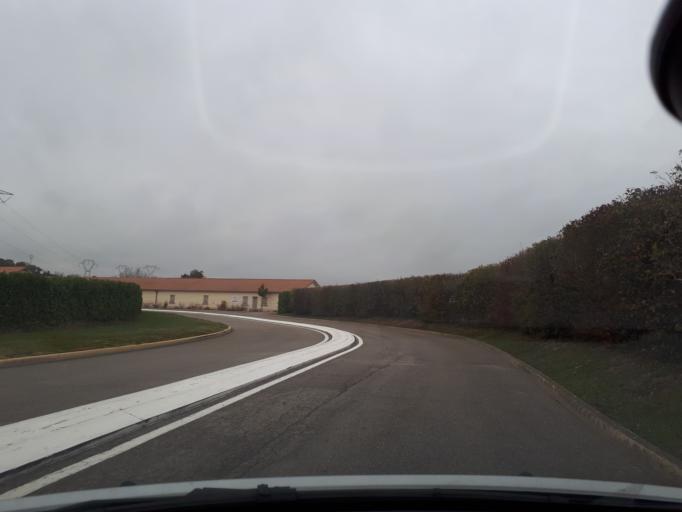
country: FR
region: Rhone-Alpes
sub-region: Departement de l'Isere
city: Champier
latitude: 45.4660
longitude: 5.2973
